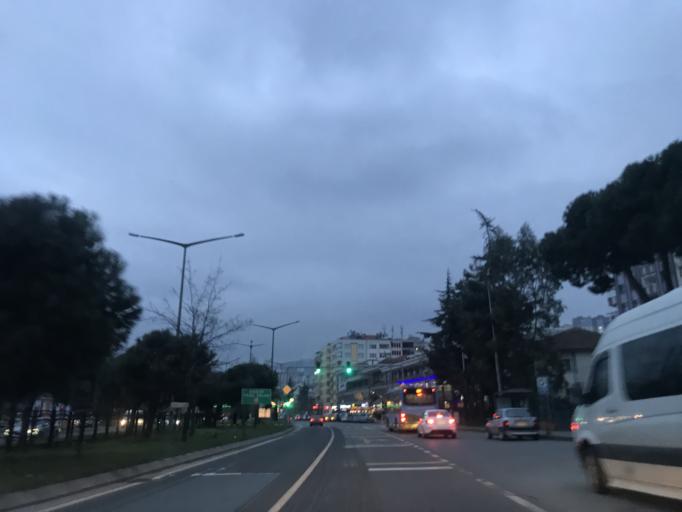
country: TR
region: Trabzon
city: Akcaabat
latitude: 41.0261
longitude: 39.5646
